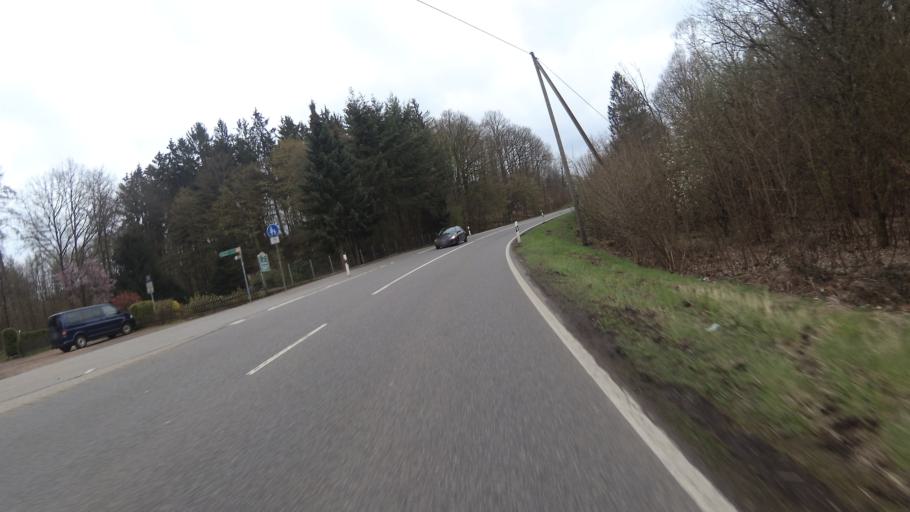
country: DE
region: Saarland
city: Merchweiler
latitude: 49.3525
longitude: 7.0761
